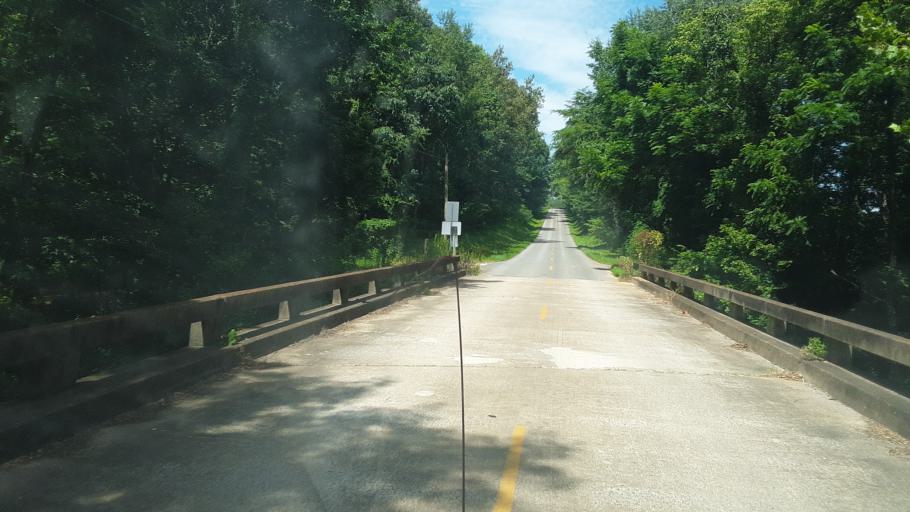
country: US
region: Kentucky
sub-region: Christian County
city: Oak Grove
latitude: 36.7313
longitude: -87.3276
